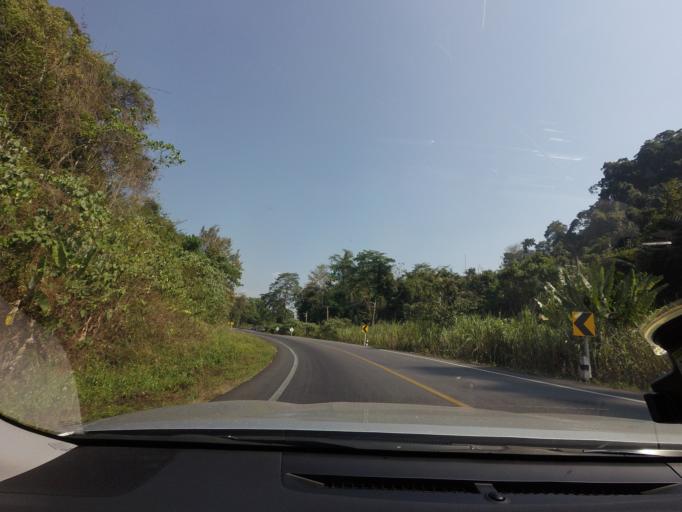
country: TH
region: Krabi
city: Plai Phraya
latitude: 8.5583
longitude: 98.7791
